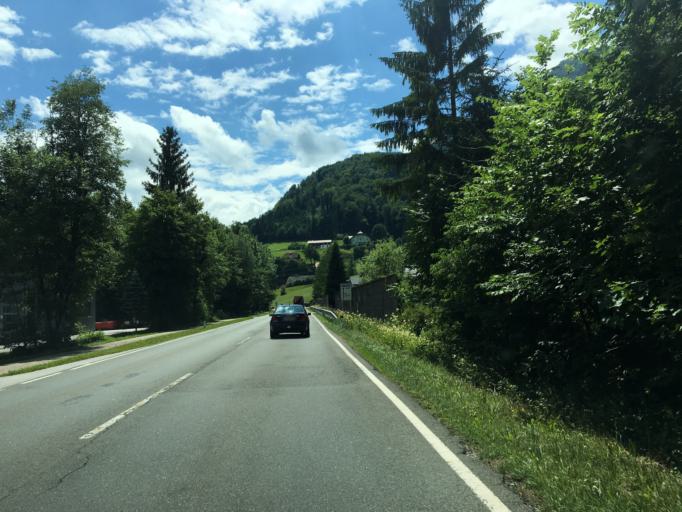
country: AT
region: Salzburg
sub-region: Politischer Bezirk Salzburg-Umgebung
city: Ebenau
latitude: 47.7683
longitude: 13.1805
